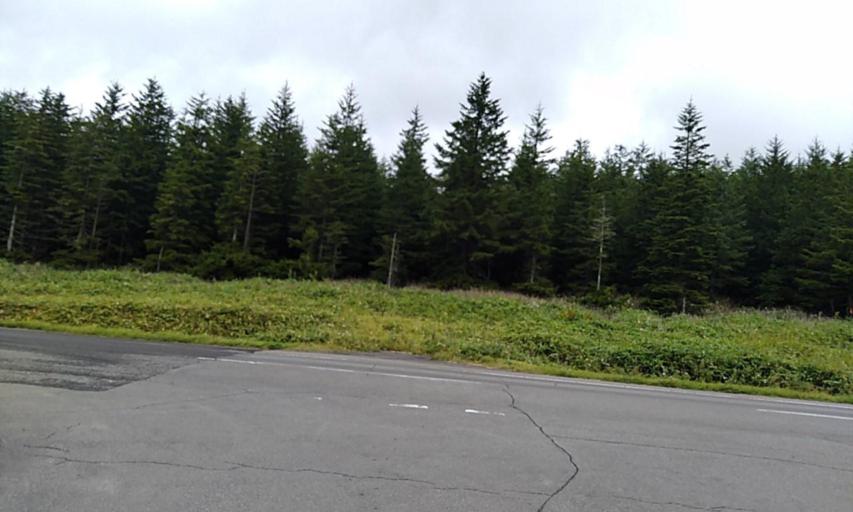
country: JP
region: Hokkaido
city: Abashiri
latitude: 43.6134
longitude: 144.5910
